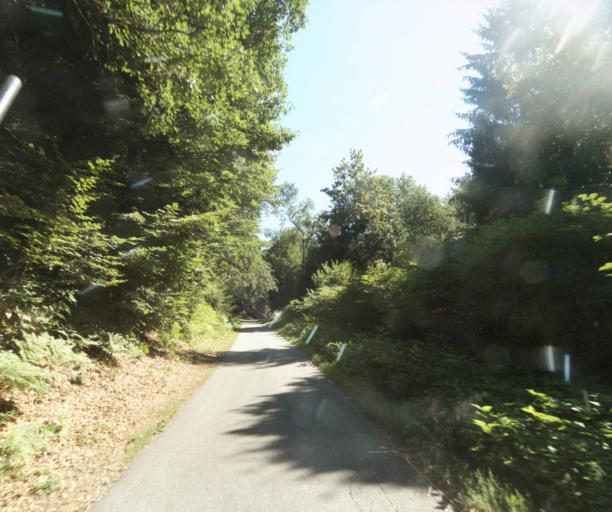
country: FR
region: Lorraine
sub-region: Departement des Vosges
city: Epinal
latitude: 48.1653
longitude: 6.4723
